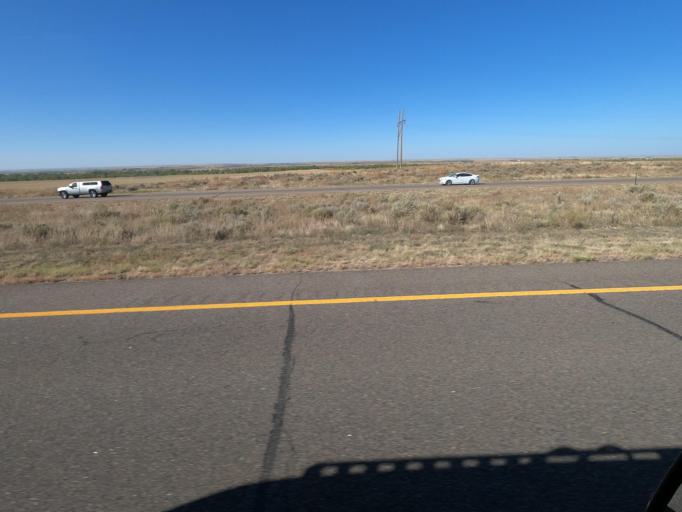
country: US
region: Nebraska
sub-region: Deuel County
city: Chappell
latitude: 40.8755
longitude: -102.6149
